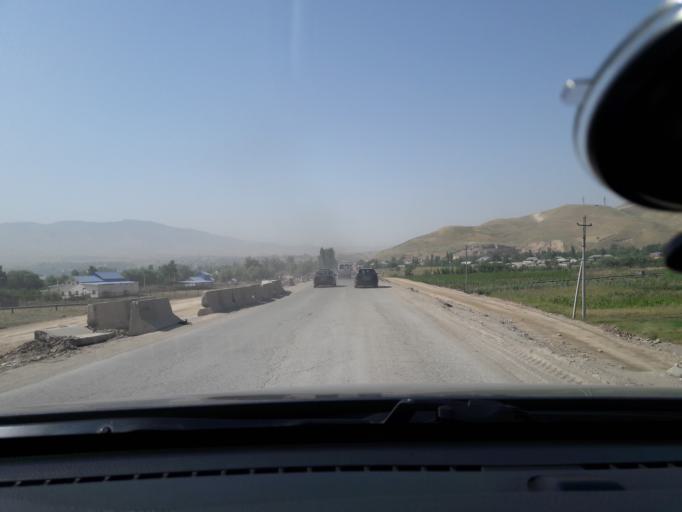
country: TJ
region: Dushanbe
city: Boshkengash
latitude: 38.4522
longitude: 68.7349
